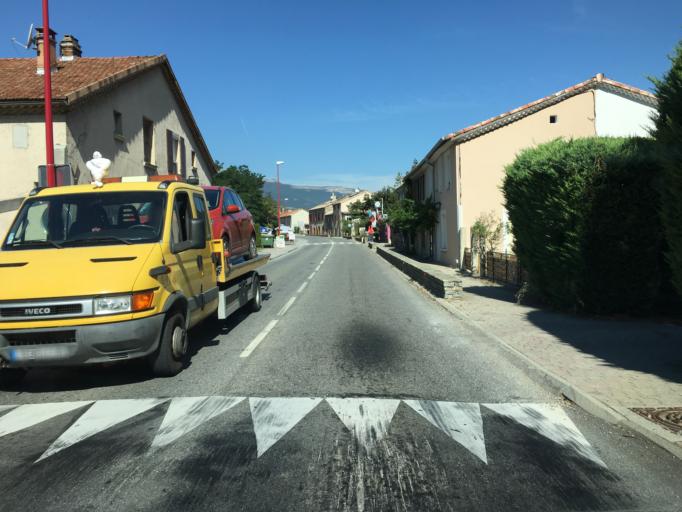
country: FR
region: Provence-Alpes-Cote d'Azur
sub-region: Departement des Hautes-Alpes
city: Laragne-Monteglin
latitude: 44.3443
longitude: 5.7740
